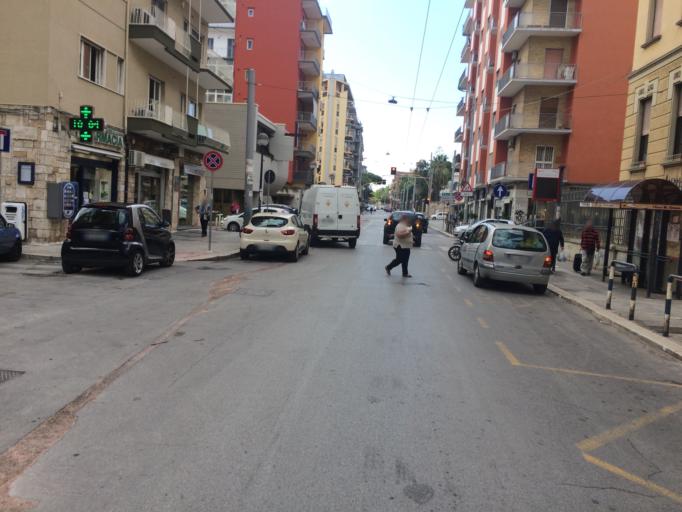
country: IT
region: Apulia
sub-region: Provincia di Bari
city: Bari
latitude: 41.1079
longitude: 16.8719
